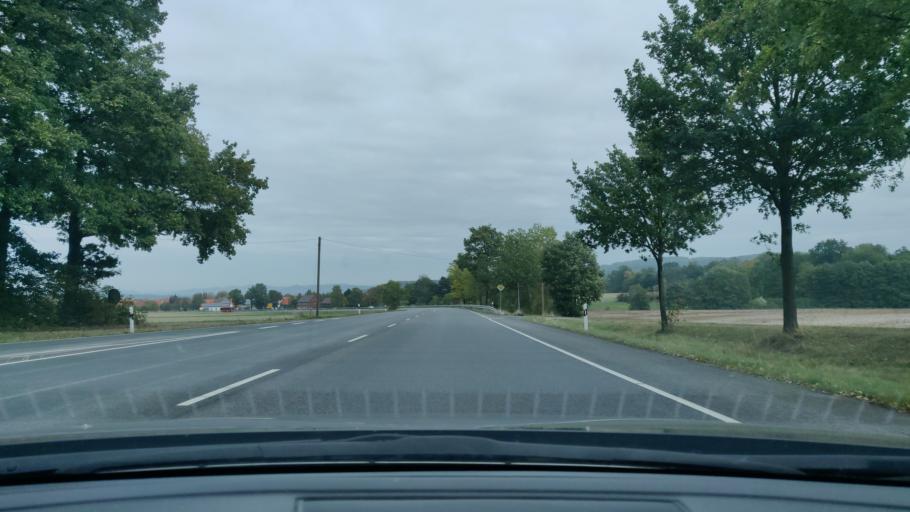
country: DE
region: Hesse
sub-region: Regierungsbezirk Kassel
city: Frielendorf
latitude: 50.9549
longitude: 9.2982
